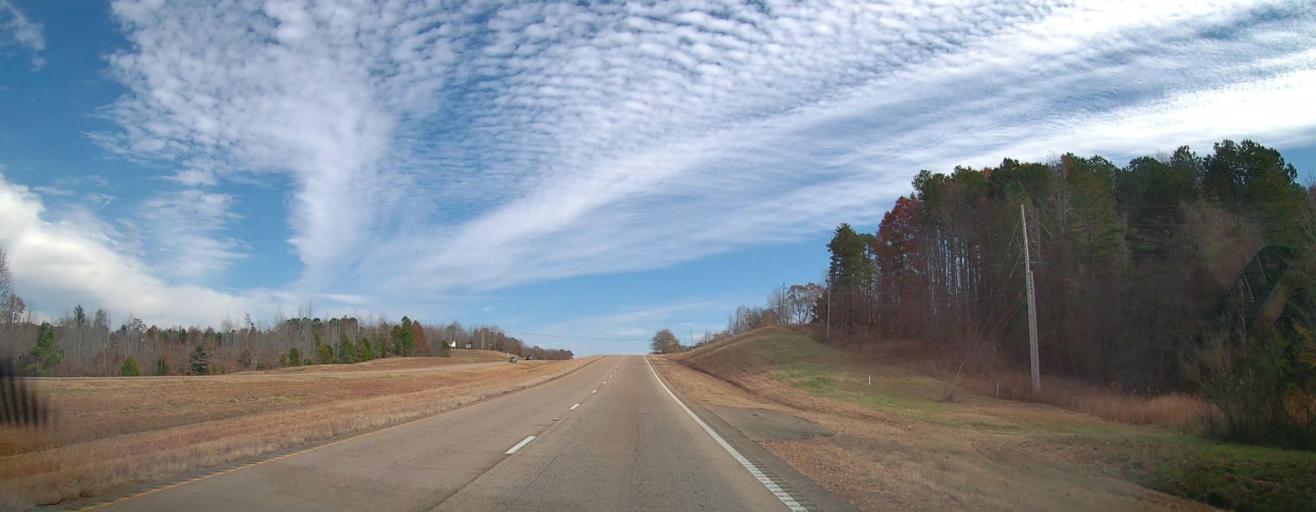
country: US
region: Mississippi
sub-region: Alcorn County
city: Corinth
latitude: 34.9310
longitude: -88.6881
